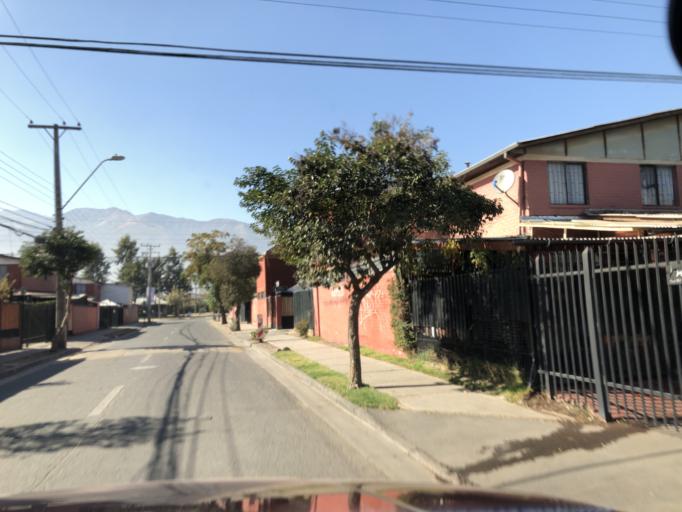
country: CL
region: Santiago Metropolitan
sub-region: Provincia de Cordillera
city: Puente Alto
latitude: -33.5655
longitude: -70.5806
